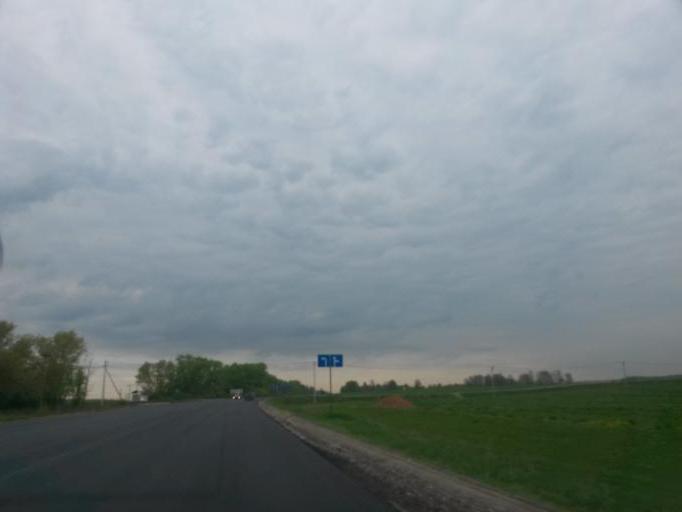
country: RU
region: Moskovskaya
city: Barybino
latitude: 55.2573
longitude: 37.8327
